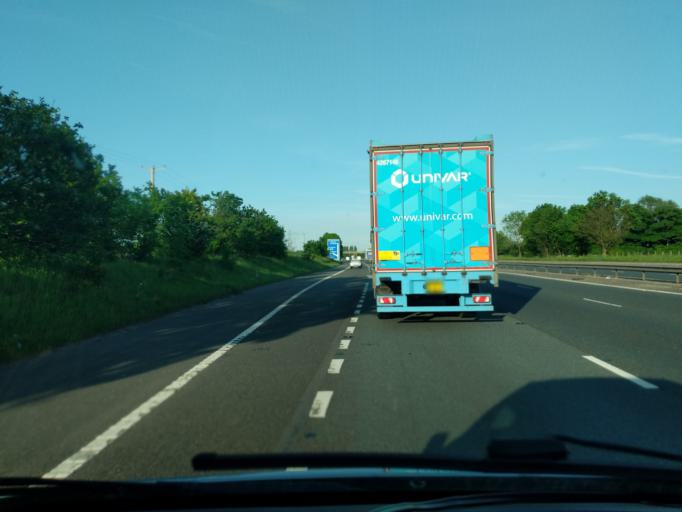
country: GB
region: England
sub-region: Knowsley
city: Whiston
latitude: 53.4005
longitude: -2.7647
